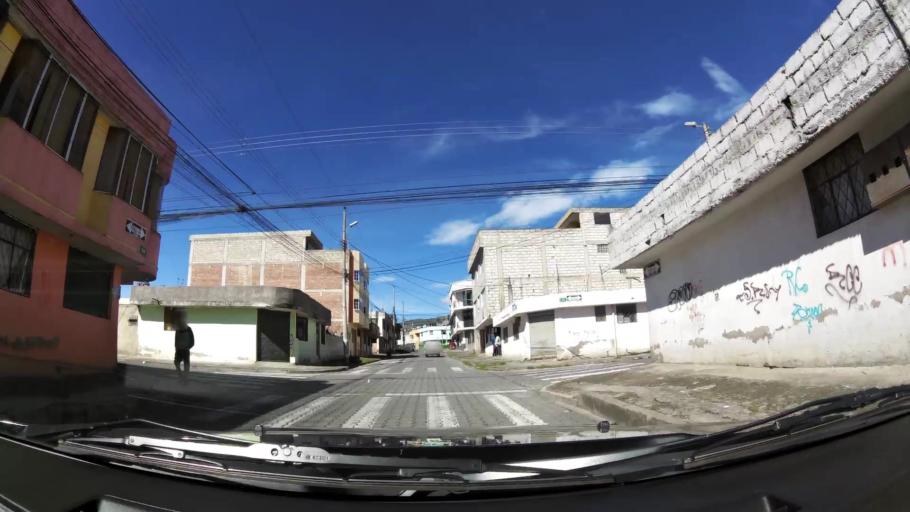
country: EC
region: Pichincha
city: Quito
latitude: -0.3026
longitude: -78.5623
